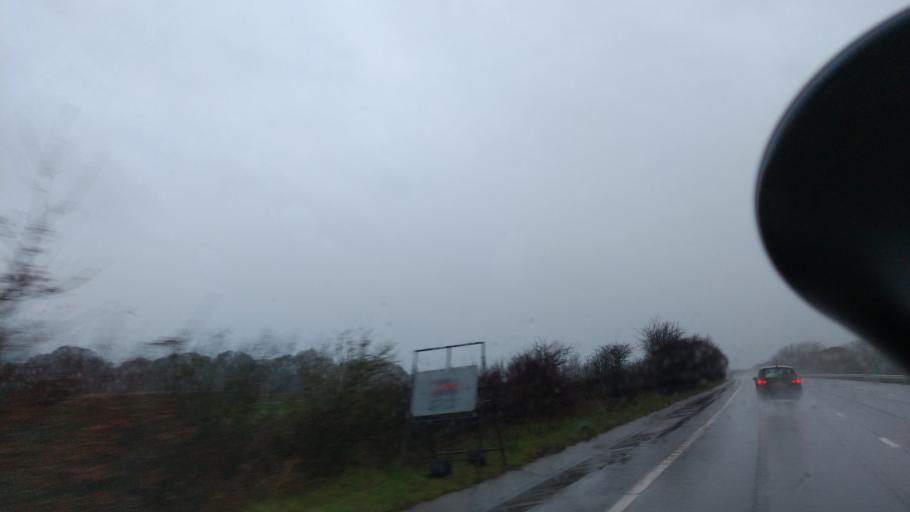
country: GB
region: England
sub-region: West Sussex
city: Goring-by-Sea
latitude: 50.8394
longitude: -0.4644
